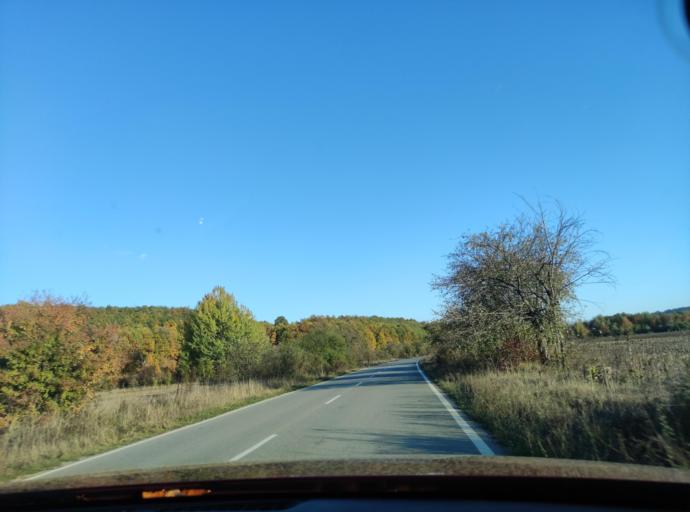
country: BG
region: Montana
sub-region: Obshtina Chiprovtsi
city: Chiprovtsi
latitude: 43.4110
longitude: 23.0460
